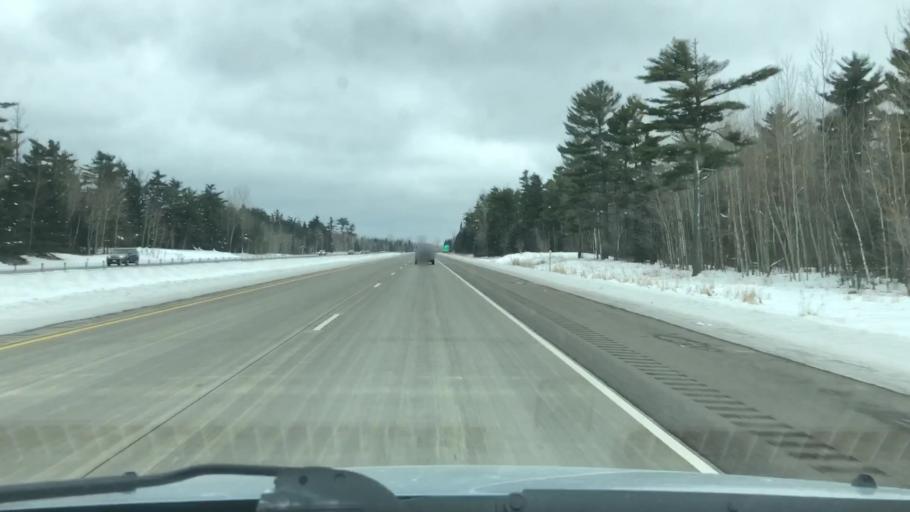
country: US
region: Minnesota
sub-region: Carlton County
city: Esko
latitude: 46.6988
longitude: -92.3299
